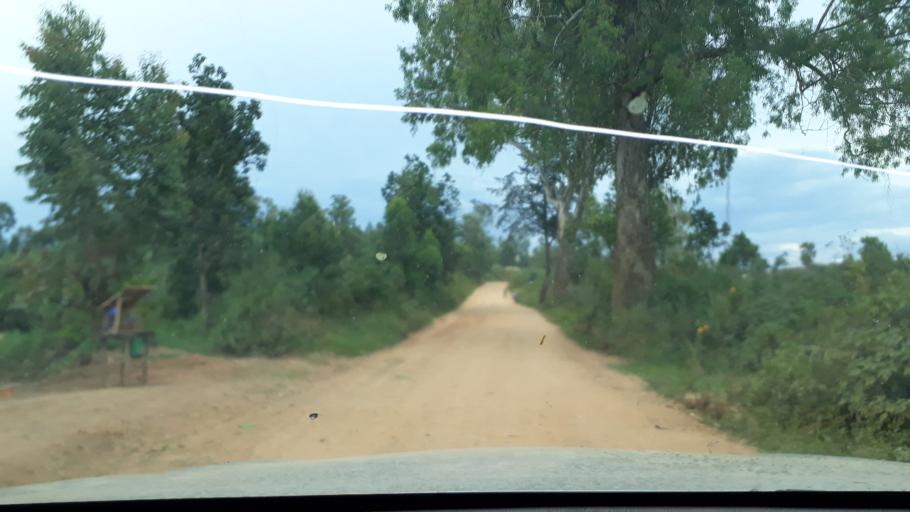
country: CD
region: Eastern Province
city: Bunia
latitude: 1.8561
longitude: 30.4781
